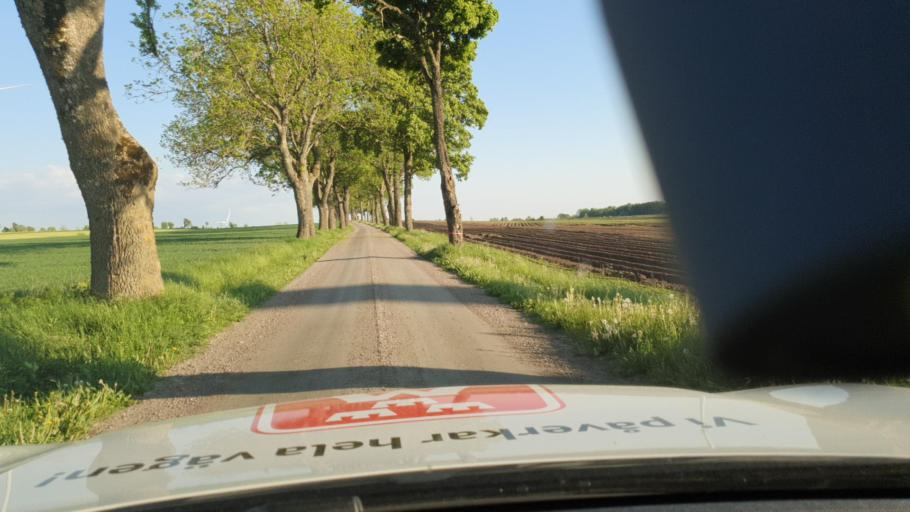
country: SE
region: Vaestra Goetaland
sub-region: Falkopings Kommun
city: Akarp
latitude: 58.1446
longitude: 13.6996
